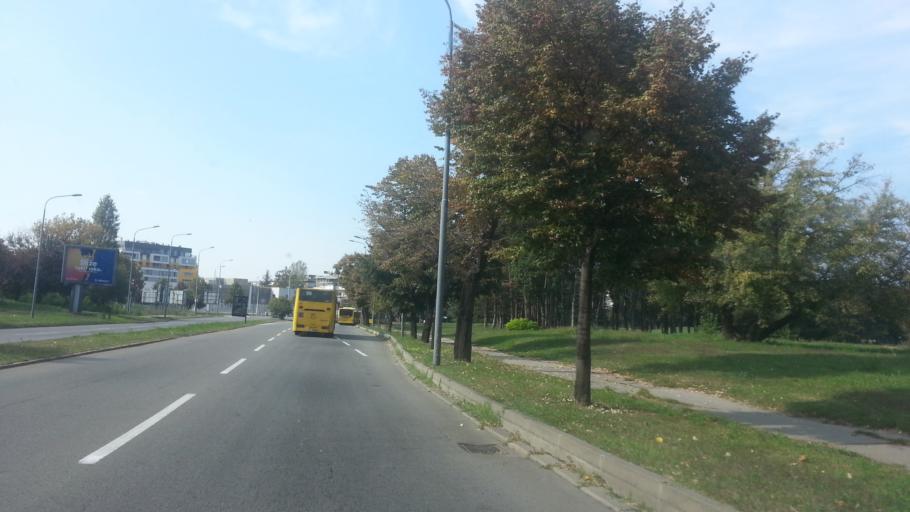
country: RS
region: Central Serbia
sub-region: Belgrade
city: Novi Beograd
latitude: 44.8244
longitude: 20.4226
